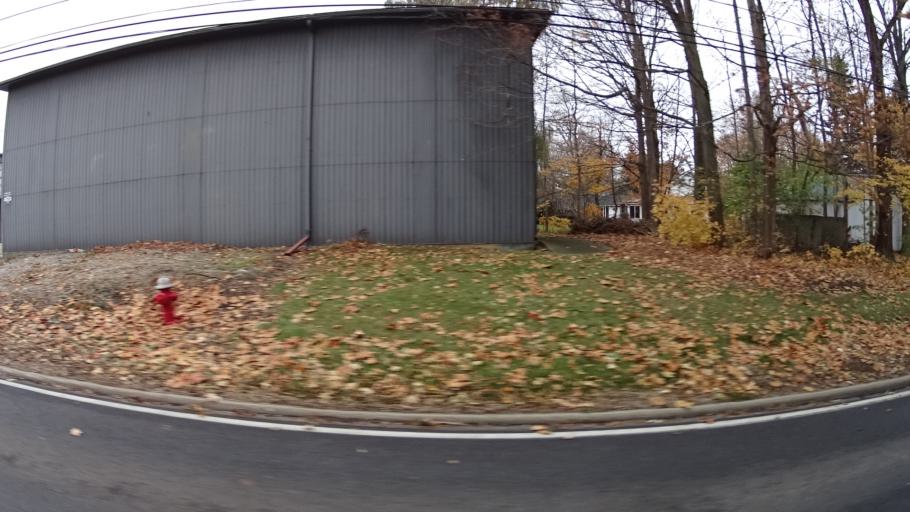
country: US
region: Ohio
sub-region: Lorain County
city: Sheffield
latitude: 41.4200
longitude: -82.0969
